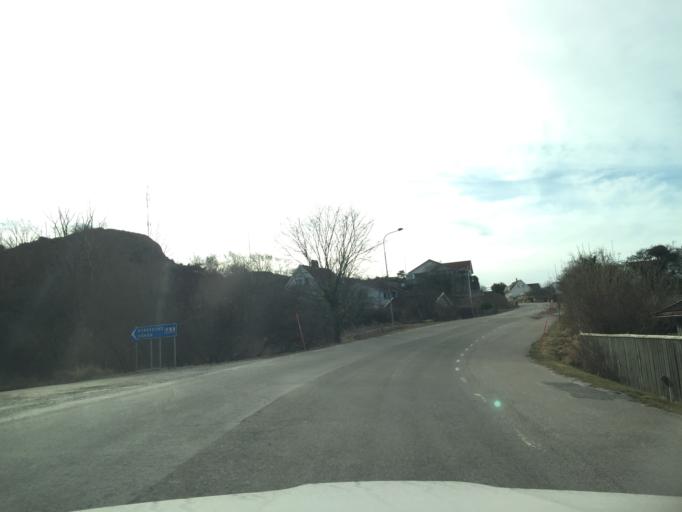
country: SE
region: Vaestra Goetaland
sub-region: Tjorns Kommun
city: Skaerhamn
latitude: 58.0181
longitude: 11.5219
